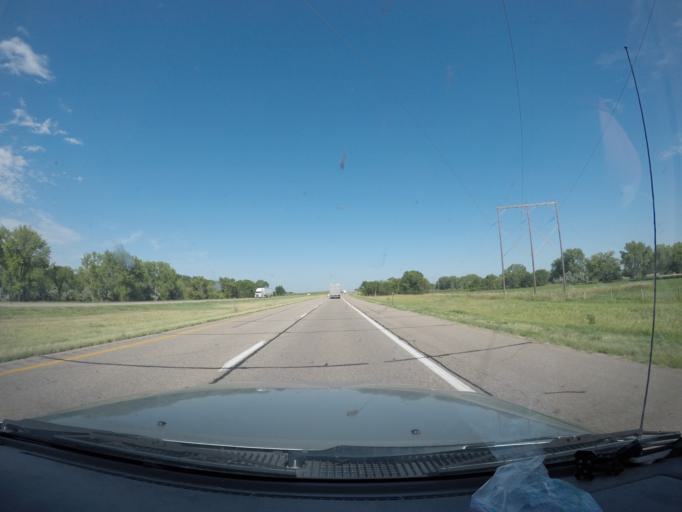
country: US
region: Nebraska
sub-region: Phelps County
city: Holdrege
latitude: 40.6908
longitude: -99.3495
